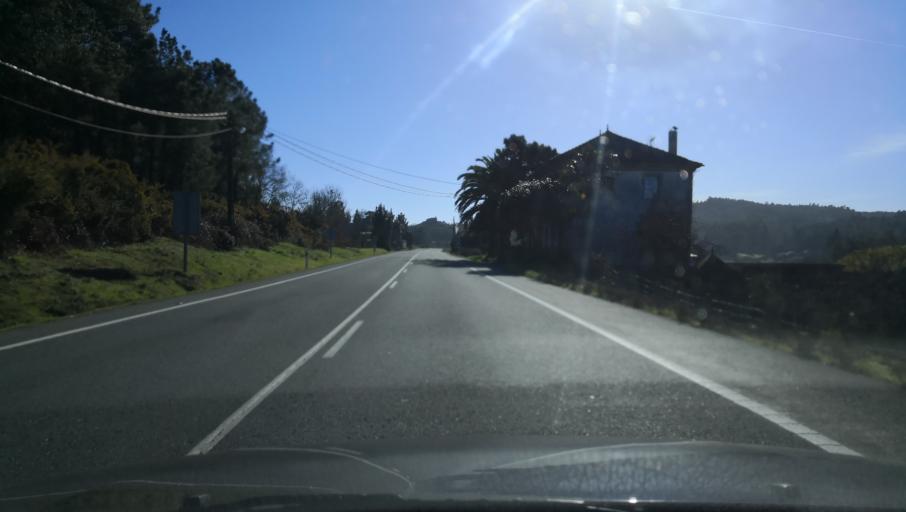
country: ES
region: Galicia
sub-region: Provincia da Coruna
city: Ribeira
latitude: 42.7521
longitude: -8.3523
